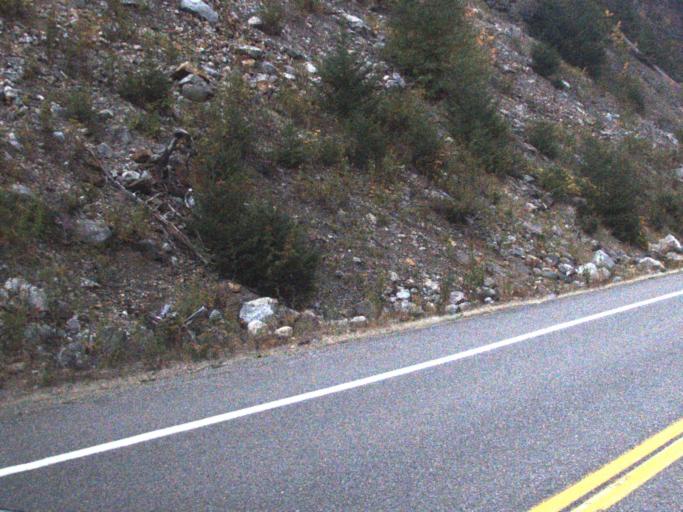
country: US
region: Washington
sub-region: Snohomish County
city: Darrington
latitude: 48.6818
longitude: -120.8831
